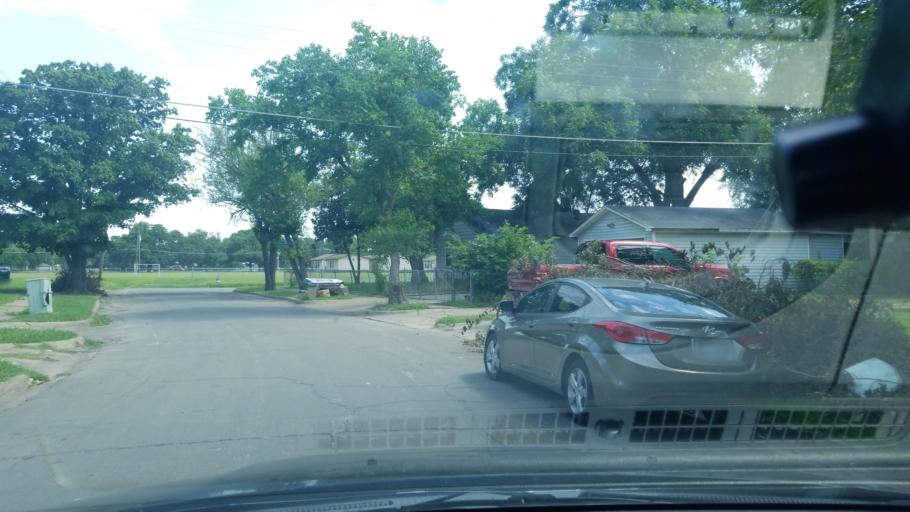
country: US
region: Texas
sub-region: Dallas County
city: Balch Springs
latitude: 32.7409
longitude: -96.6902
